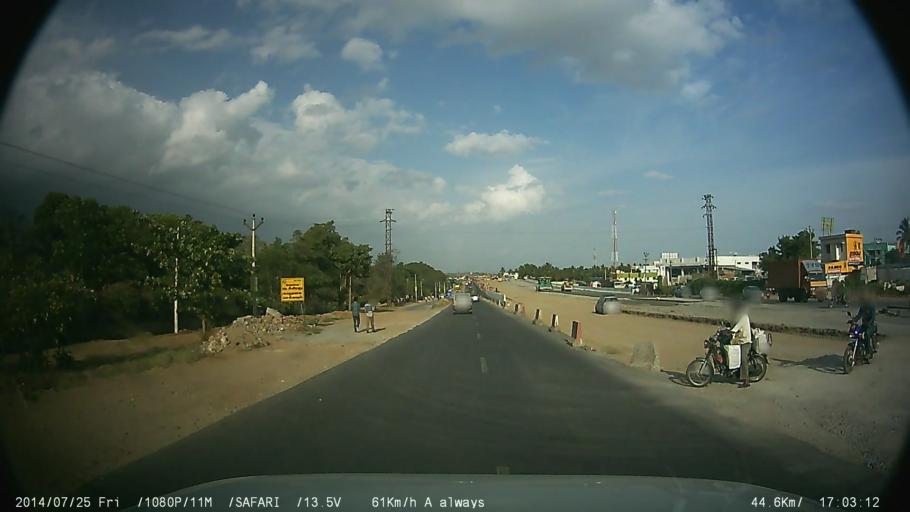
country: IN
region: Tamil Nadu
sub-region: Krishnagiri
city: Hosur
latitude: 12.7180
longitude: 77.8747
